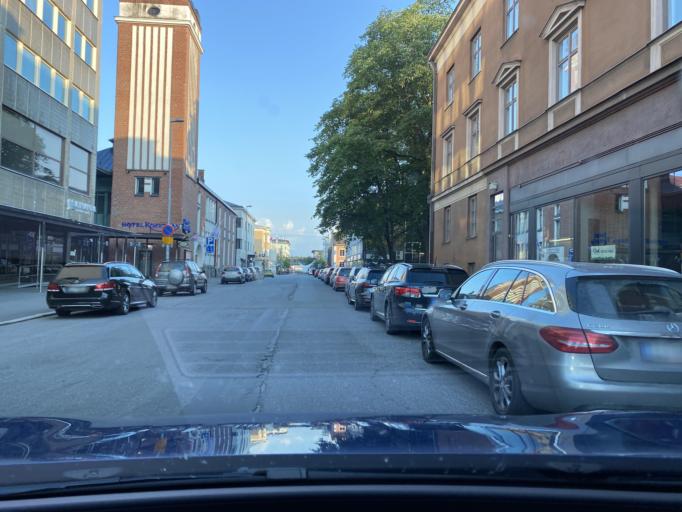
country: FI
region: Central Ostrobothnia
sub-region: Kokkola
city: Kokkola
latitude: 63.8385
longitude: 23.1324
